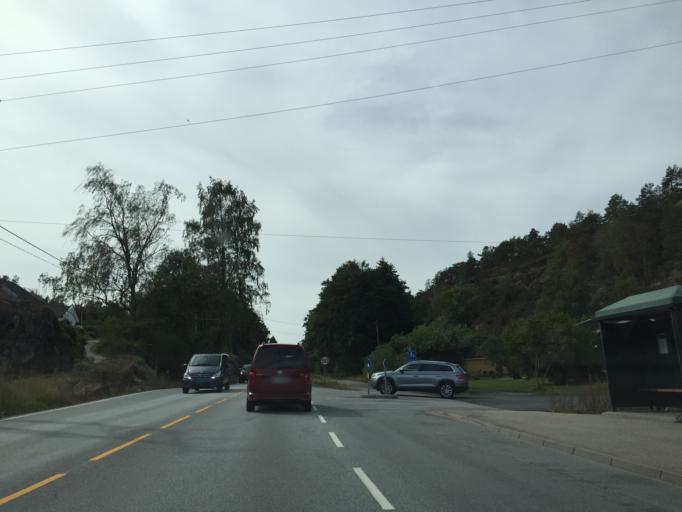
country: NO
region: Ostfold
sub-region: Fredrikstad
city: Fredrikstad
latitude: 59.1100
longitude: 10.9098
